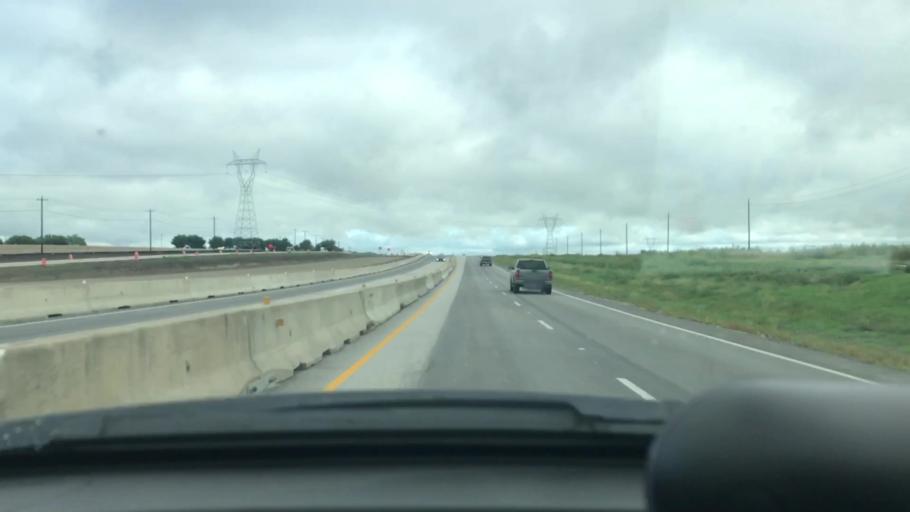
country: US
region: Texas
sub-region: Collin County
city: Anna
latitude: 33.3661
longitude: -96.5827
